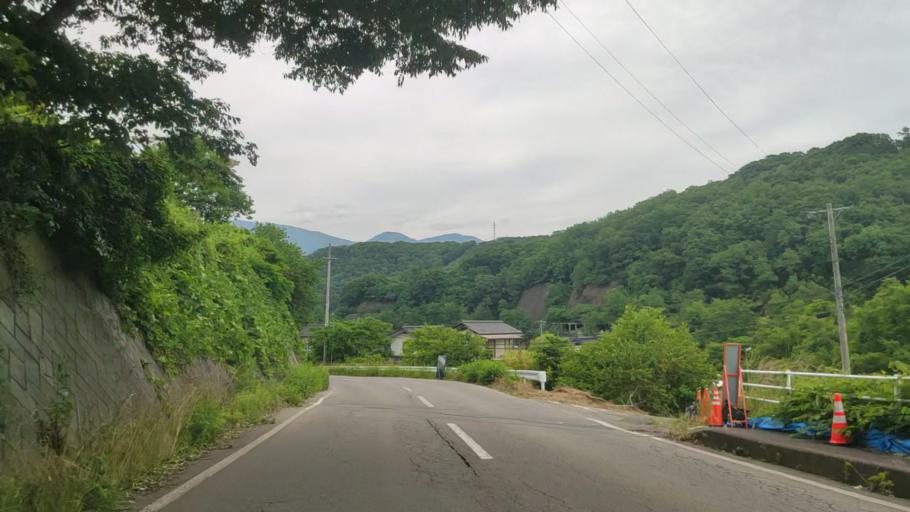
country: JP
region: Nagano
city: Kamimaruko
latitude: 36.3283
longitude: 138.3440
